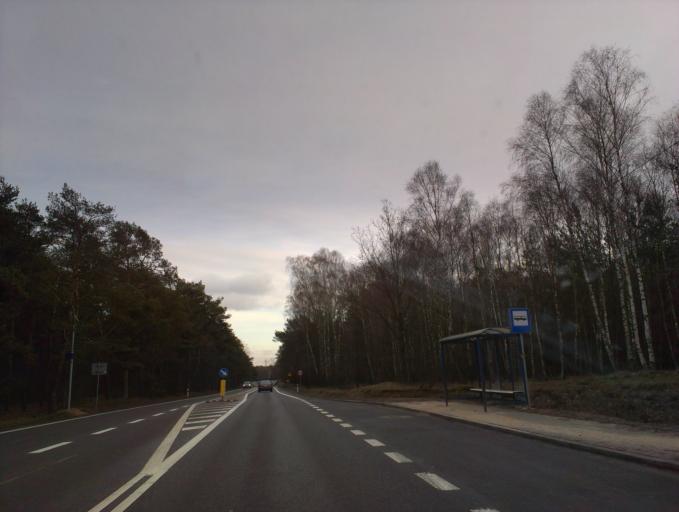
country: PL
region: Masovian Voivodeship
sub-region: Powiat sierpecki
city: Sierpc
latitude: 52.8706
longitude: 19.6240
